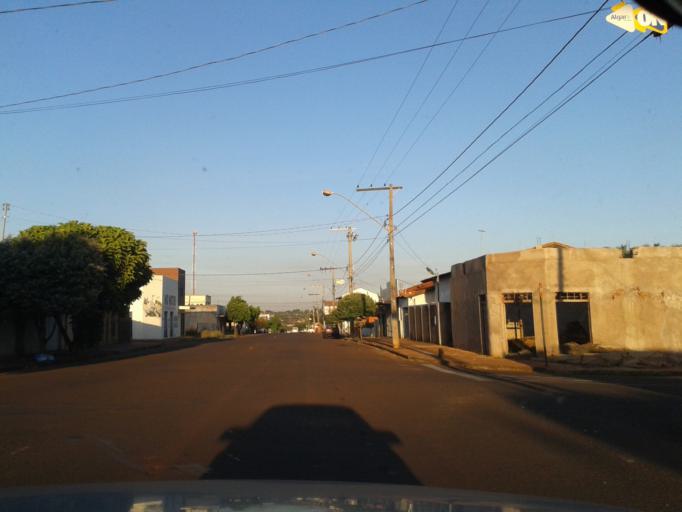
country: BR
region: Minas Gerais
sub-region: Ituiutaba
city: Ituiutaba
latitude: -18.9835
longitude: -49.4655
